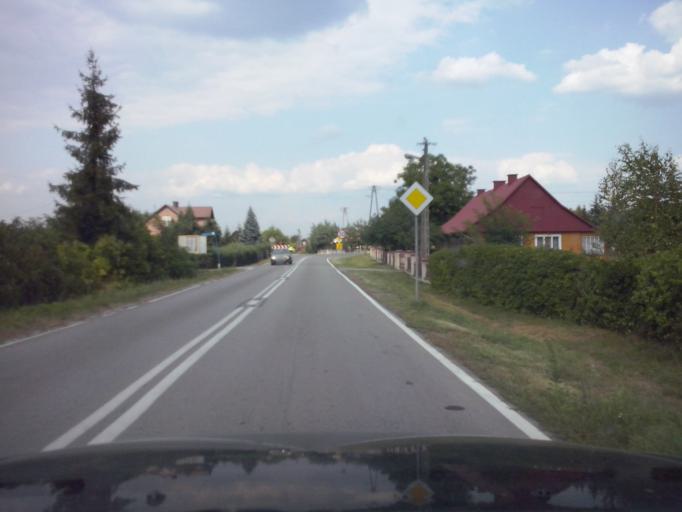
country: PL
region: Subcarpathian Voivodeship
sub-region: Powiat nizanski
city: Bieliny
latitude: 50.3999
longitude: 22.2992
